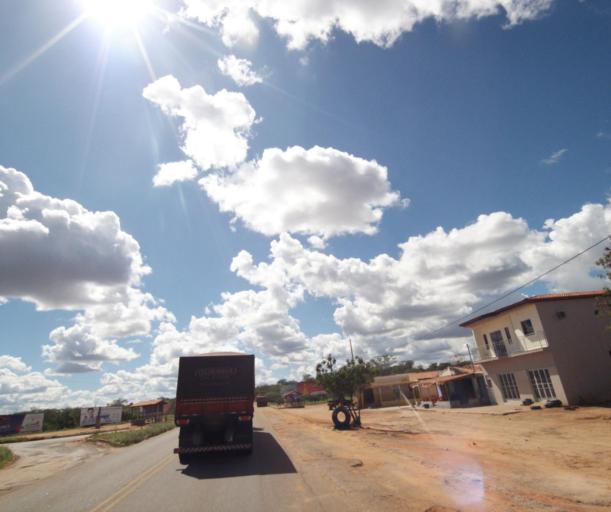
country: BR
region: Bahia
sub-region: Caetite
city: Caetite
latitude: -14.1699
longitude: -42.2291
